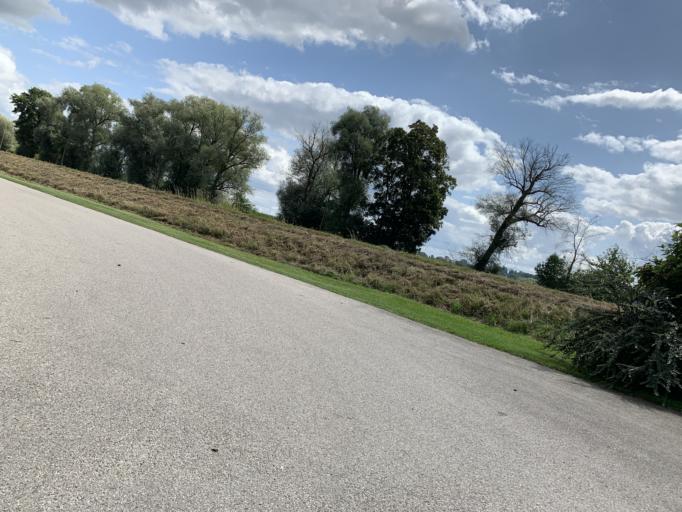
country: DE
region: Bavaria
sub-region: Upper Bavaria
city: Zolling
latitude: 48.4502
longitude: 11.7782
